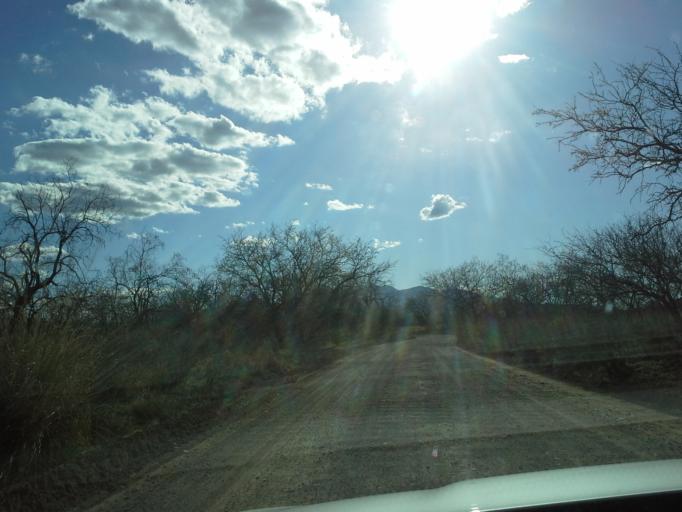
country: US
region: Arizona
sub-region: Pima County
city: Corona de Tucson
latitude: 31.7371
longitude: -110.6685
